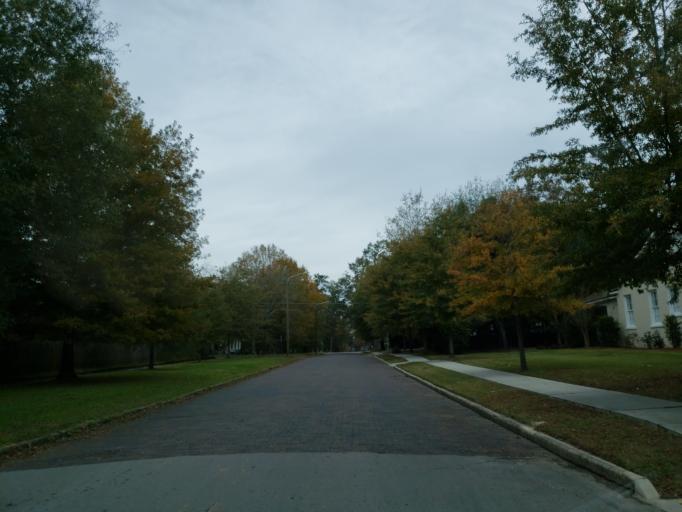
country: US
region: Mississippi
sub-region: Forrest County
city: Hattiesburg
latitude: 31.3229
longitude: -89.2997
